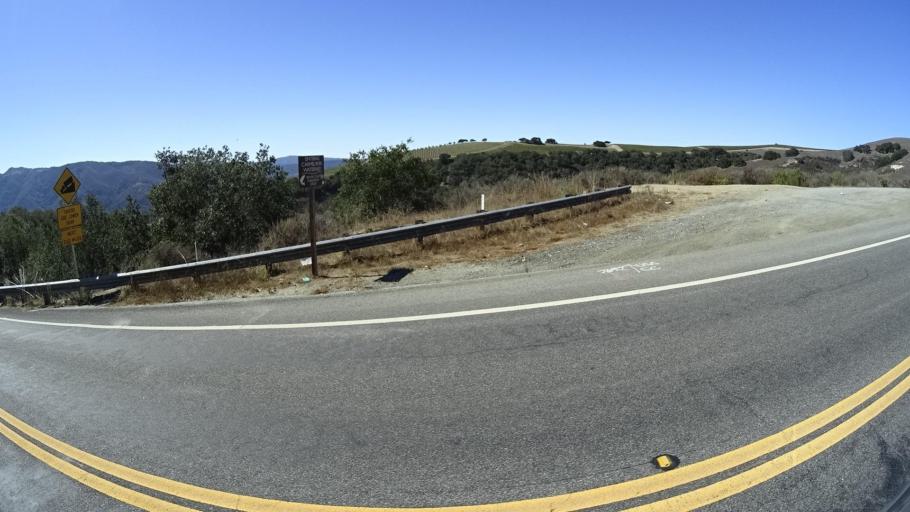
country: US
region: California
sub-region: Monterey County
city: Carmel Valley Village
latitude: 36.5258
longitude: -121.7544
